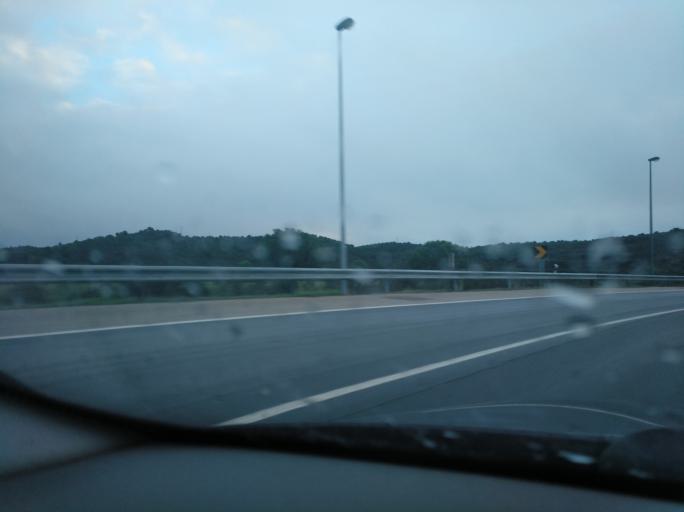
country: PT
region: Faro
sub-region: Castro Marim
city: Castro Marim
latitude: 37.3292
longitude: -7.4857
